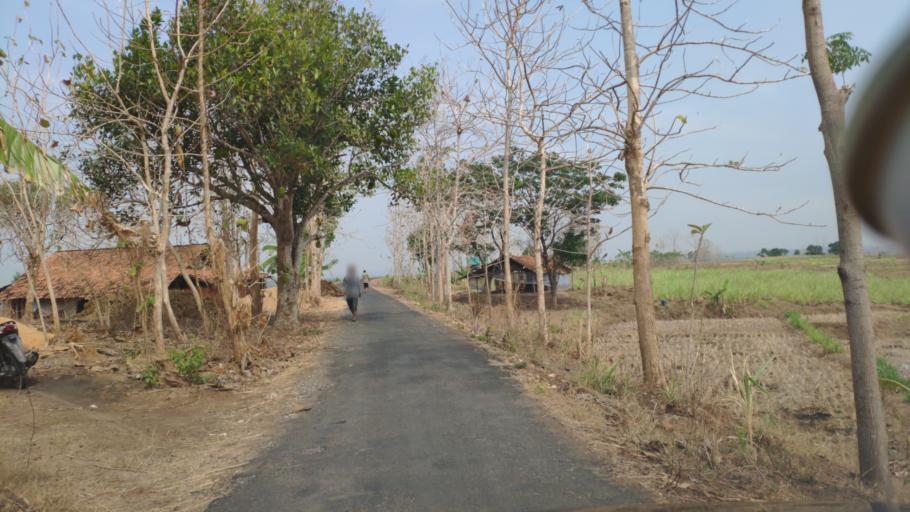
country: ID
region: Central Java
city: Wantil
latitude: -6.9712
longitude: 111.3320
